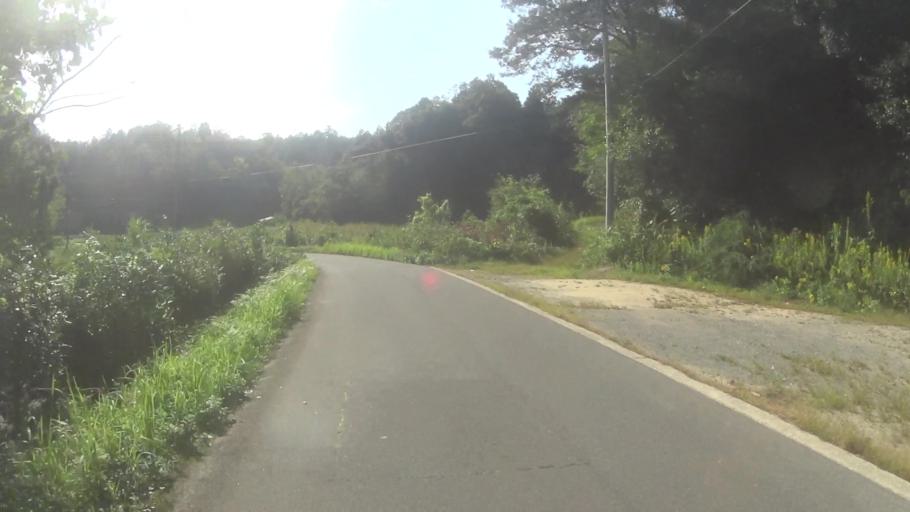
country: JP
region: Kyoto
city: Miyazu
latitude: 35.6593
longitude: 135.0672
